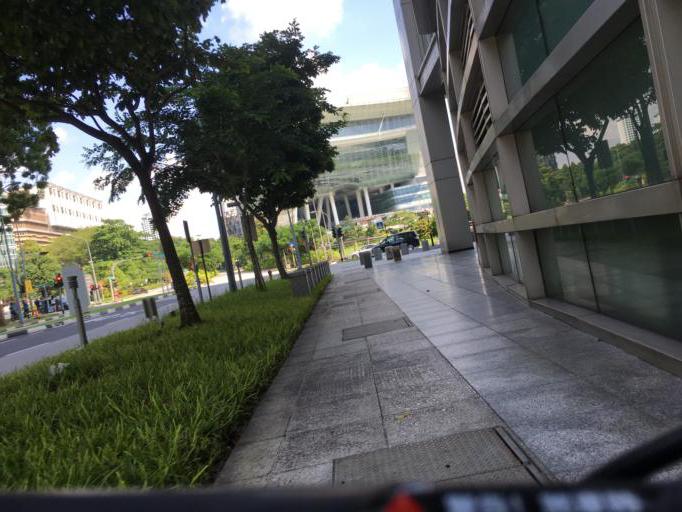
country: SG
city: Singapore
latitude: 1.3051
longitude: 103.7906
